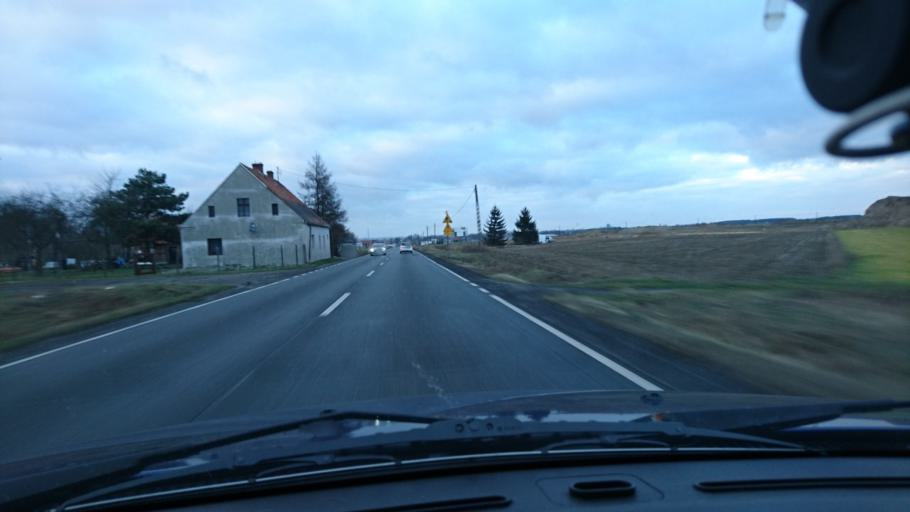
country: PL
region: Greater Poland Voivodeship
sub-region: Powiat kepinski
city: Baranow
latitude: 51.2542
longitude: 18.0121
